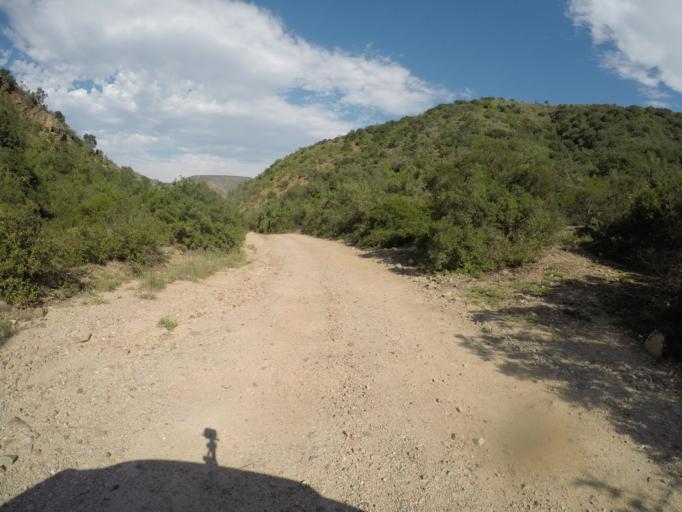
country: ZA
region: Eastern Cape
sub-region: Cacadu District Municipality
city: Kareedouw
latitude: -33.6556
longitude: 24.4015
